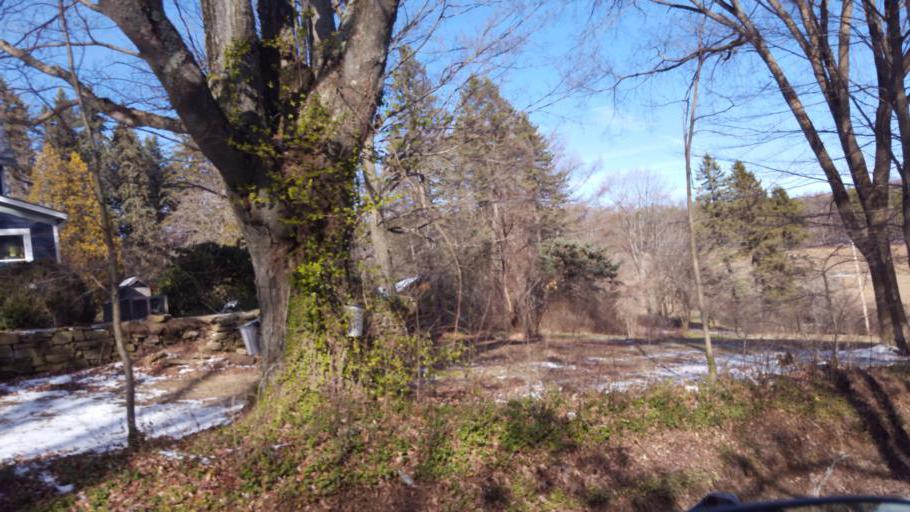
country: US
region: New York
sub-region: Allegany County
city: Wellsville
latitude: 42.0838
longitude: -77.9780
